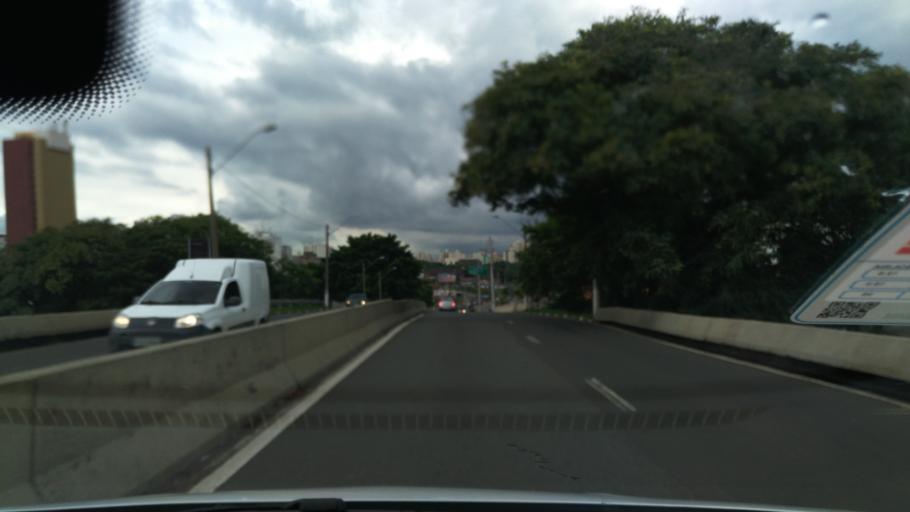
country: BR
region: Sao Paulo
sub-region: Campinas
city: Campinas
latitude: -22.9053
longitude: -47.0717
